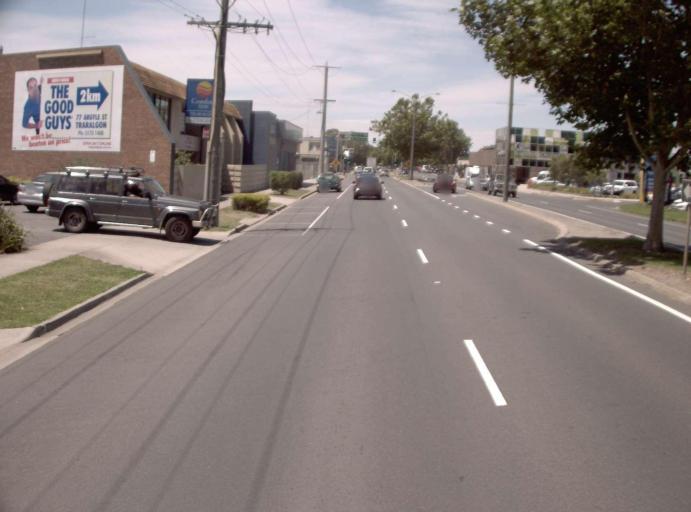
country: AU
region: Victoria
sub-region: Latrobe
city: Traralgon
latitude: -38.1987
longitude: 146.5357
